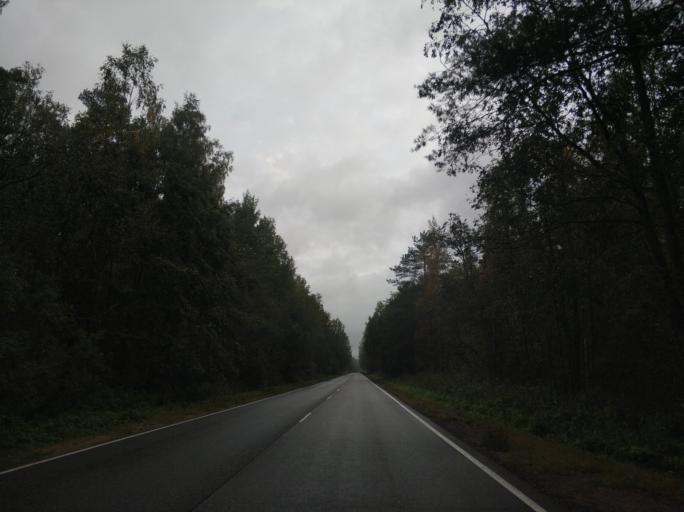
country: RU
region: Leningrad
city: Borisova Griva
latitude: 60.1539
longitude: 30.9327
